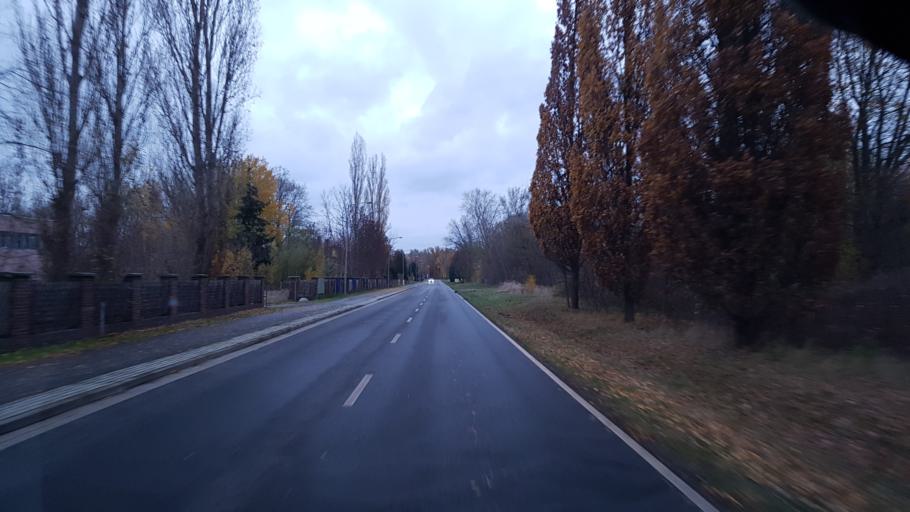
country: DE
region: Brandenburg
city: Lauchhammer
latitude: 51.4839
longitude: 13.7325
